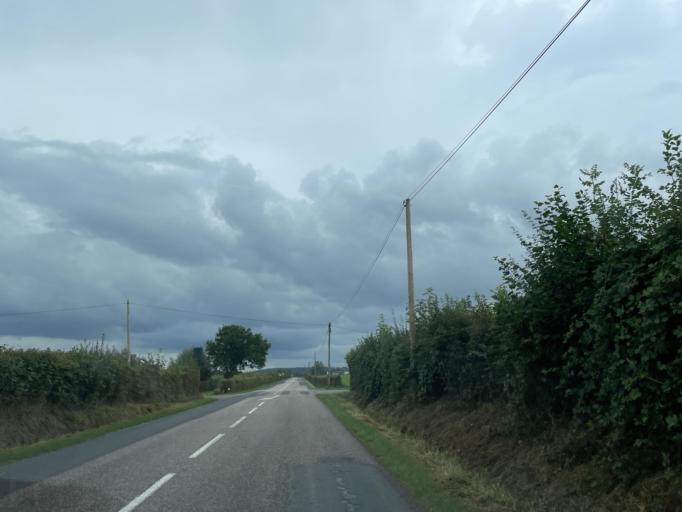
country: FR
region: Haute-Normandie
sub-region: Departement de la Seine-Maritime
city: Neufchatel-en-Bray
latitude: 49.6869
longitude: 1.4306
